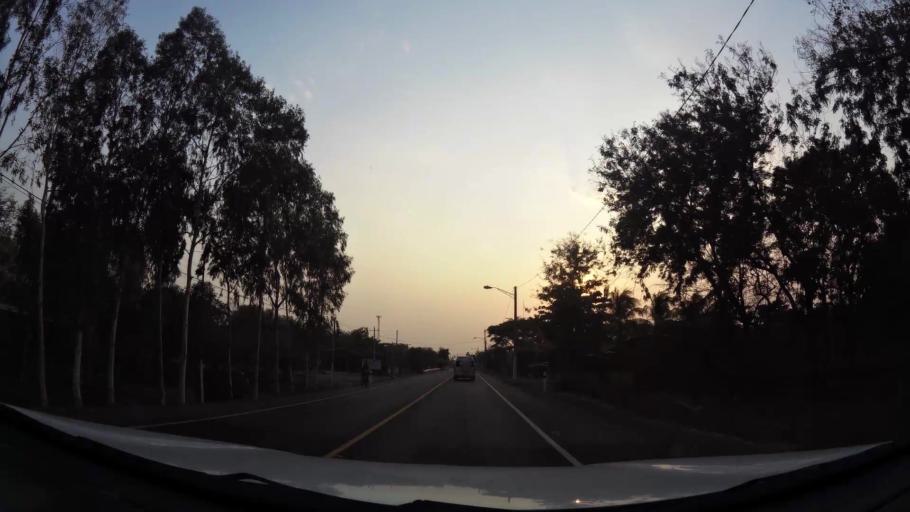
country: NI
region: Leon
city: La Paz Centro
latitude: 12.3350
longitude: -86.6713
